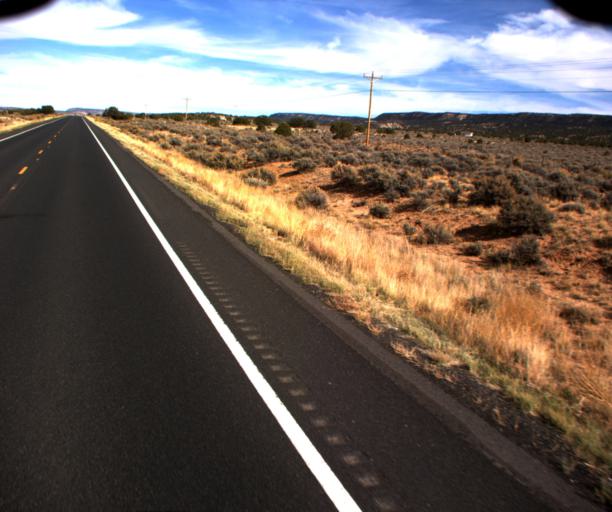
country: US
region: Arizona
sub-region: Navajo County
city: Kayenta
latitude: 36.5081
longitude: -110.6065
